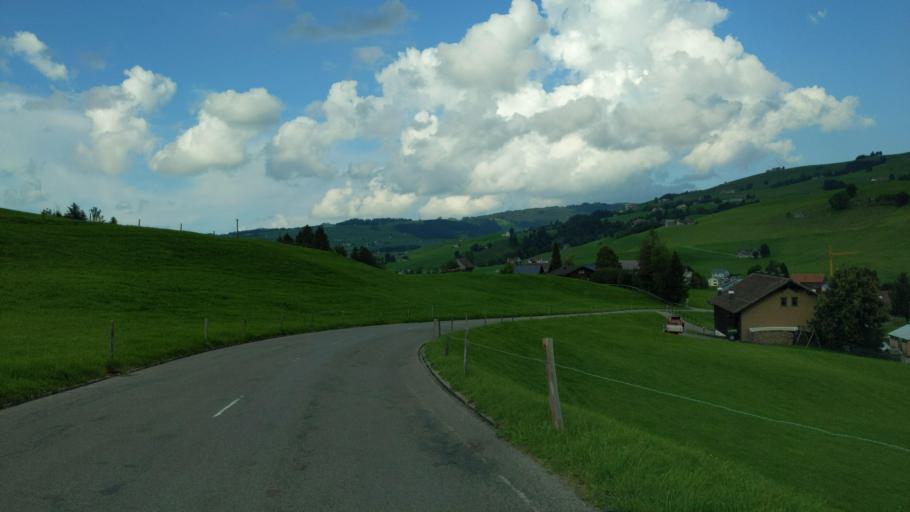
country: CH
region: Appenzell Innerrhoden
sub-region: Appenzell Inner Rhodes
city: Appenzell
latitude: 47.3058
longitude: 9.4310
